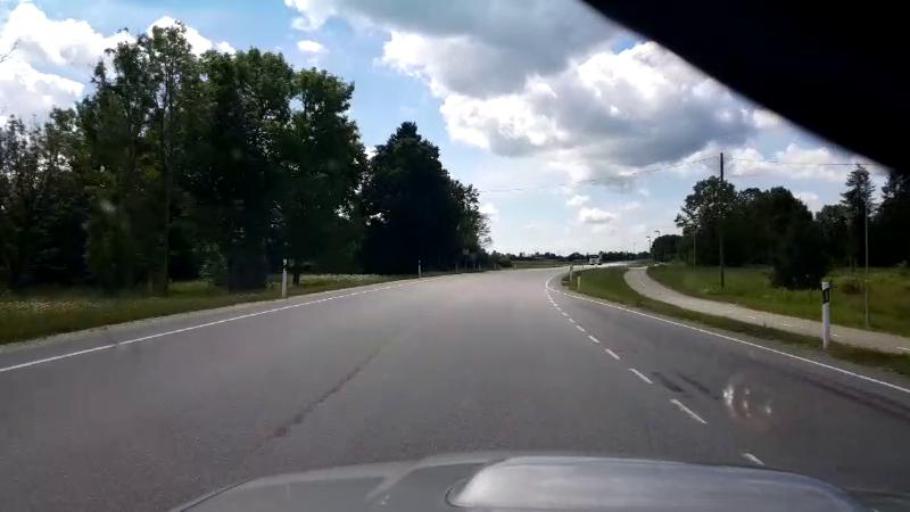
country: EE
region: Jaervamaa
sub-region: Jaerva-Jaani vald
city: Jarva-Jaani
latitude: 59.0225
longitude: 25.7054
